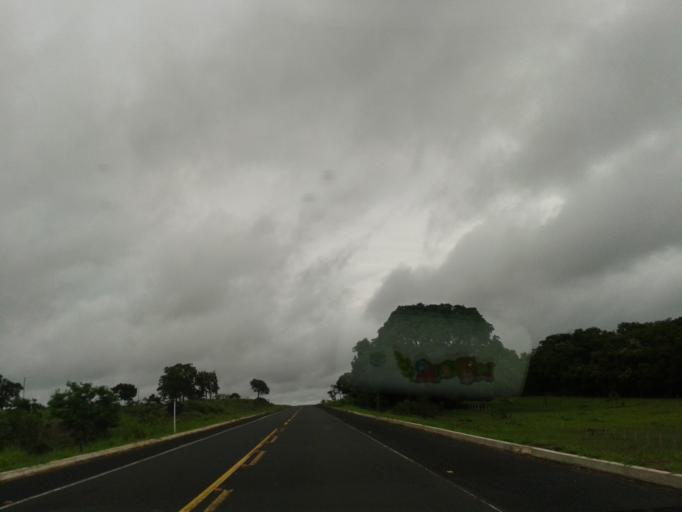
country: BR
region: Minas Gerais
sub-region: Santa Vitoria
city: Santa Vitoria
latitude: -19.2304
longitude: -50.0182
